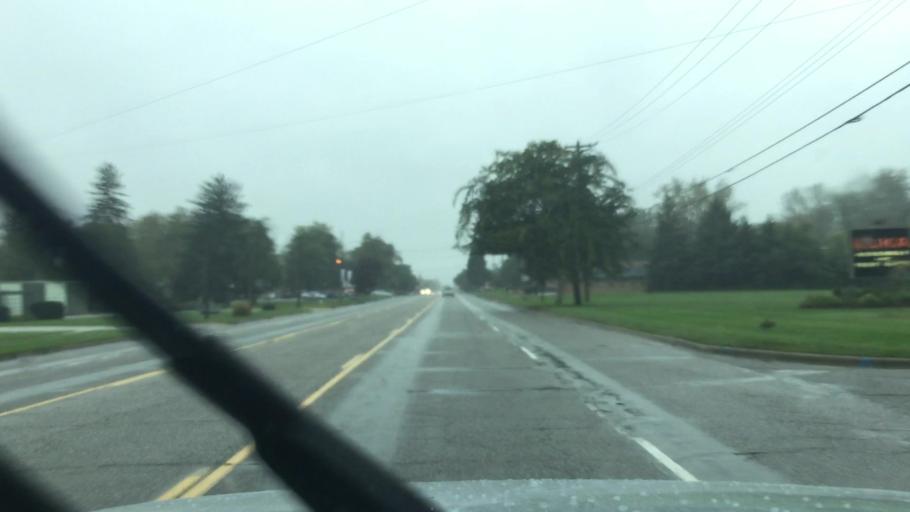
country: US
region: Michigan
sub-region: Saginaw County
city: Bridgeport
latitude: 43.3737
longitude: -83.8921
